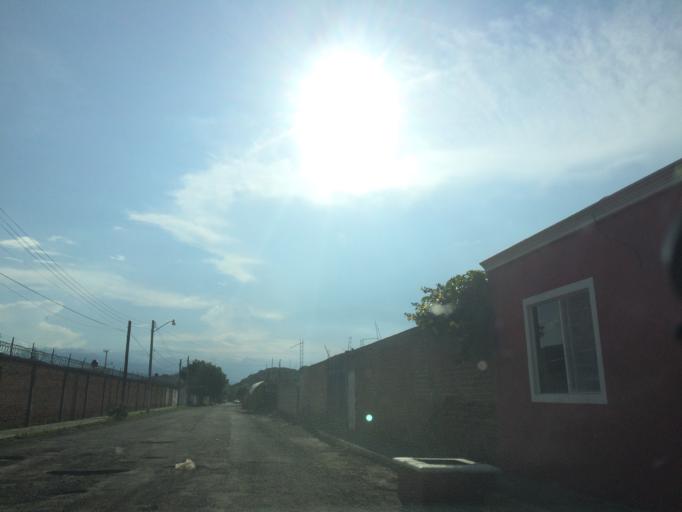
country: MX
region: Nayarit
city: Ixtlan del Rio
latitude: 21.0350
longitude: -104.3851
